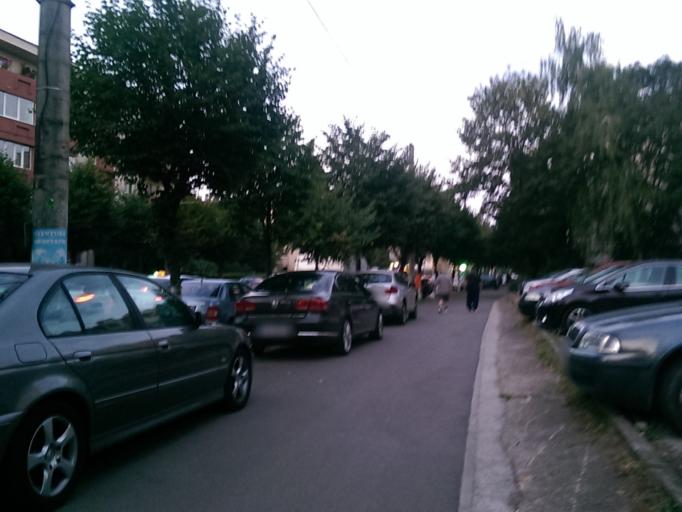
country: RO
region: Cluj
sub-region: Municipiul Cluj-Napoca
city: Cluj-Napoca
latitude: 46.7689
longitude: 23.6066
